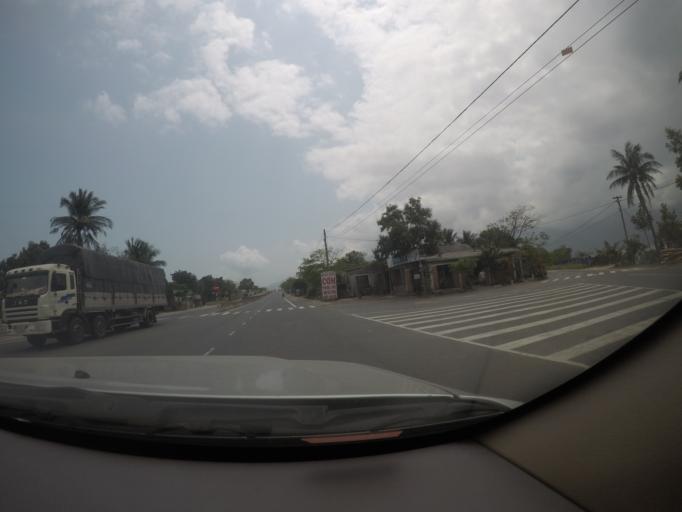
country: VN
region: Thua Thien-Hue
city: Phu Loc
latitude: 16.2595
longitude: 108.0603
